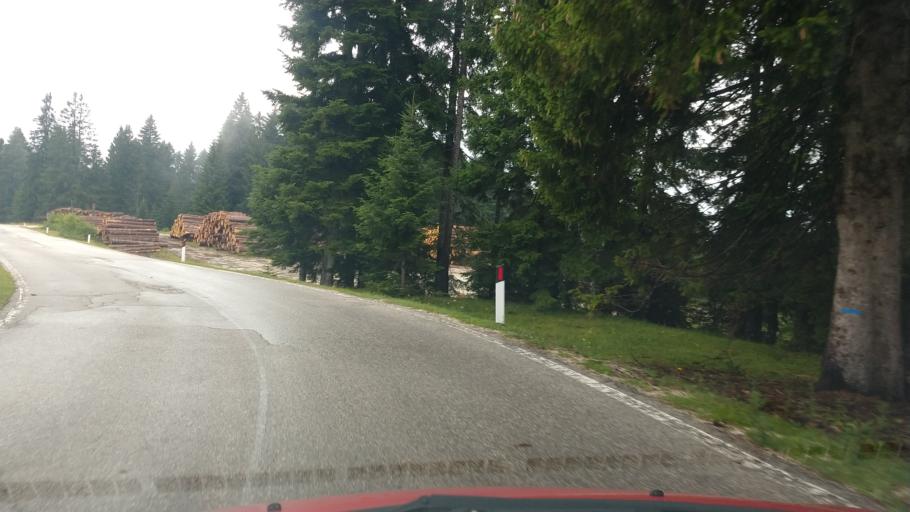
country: IT
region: Veneto
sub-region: Provincia di Vicenza
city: Lastebasse
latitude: 45.9113
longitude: 11.2400
